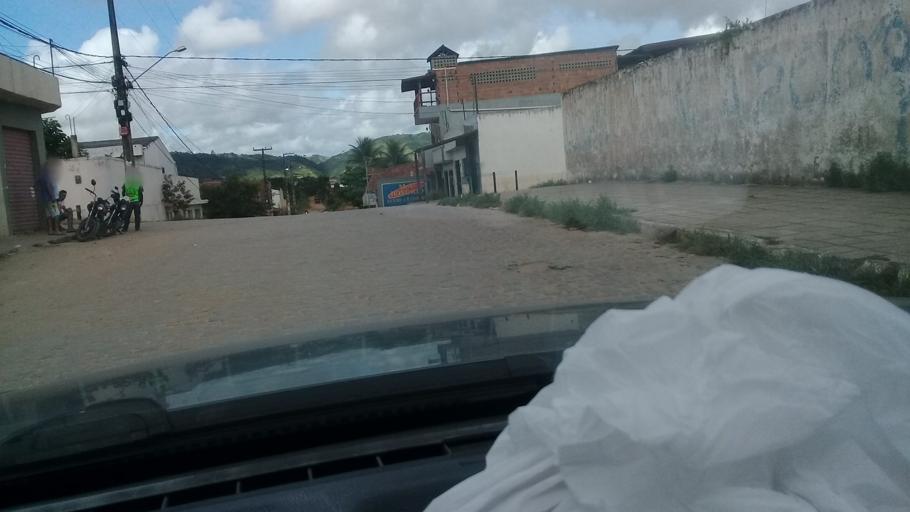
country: BR
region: Pernambuco
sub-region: Vitoria De Santo Antao
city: Vitoria de Santo Antao
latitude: -8.1302
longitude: -35.2966
